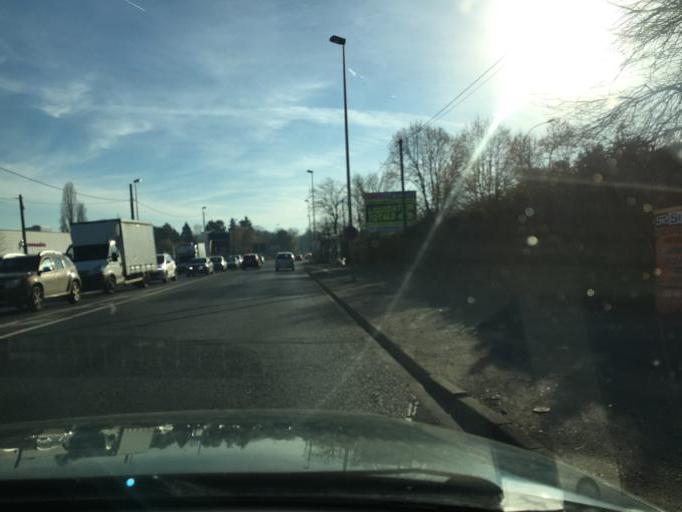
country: FR
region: Centre
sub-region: Departement du Loiret
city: Saran
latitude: 47.9544
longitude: 1.8911
